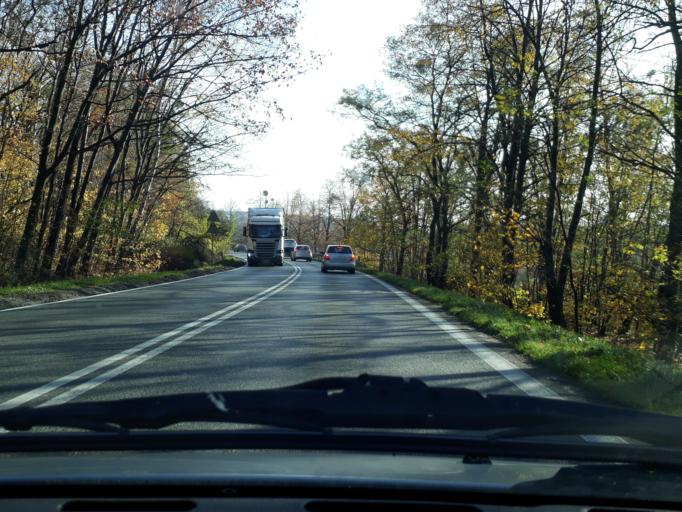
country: PL
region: Silesian Voivodeship
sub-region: Powiat tarnogorski
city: Tarnowskie Gory
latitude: 50.4408
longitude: 18.8364
